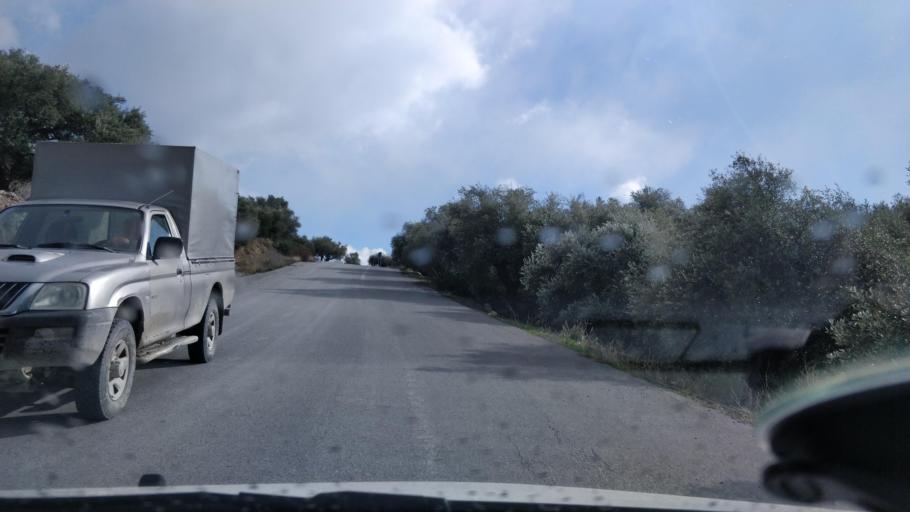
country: GR
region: Crete
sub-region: Nomos Lasithiou
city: Gra Liyia
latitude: 34.9949
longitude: 25.5121
